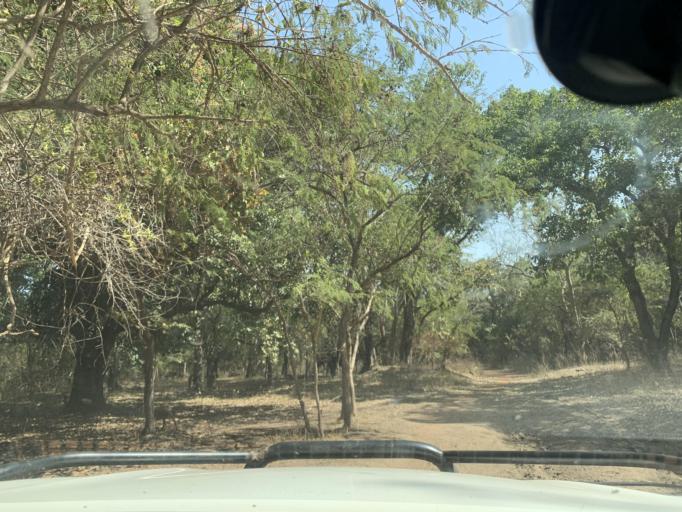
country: ML
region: Sikasso
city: Kolondieba
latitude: 10.8294
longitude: -6.7260
